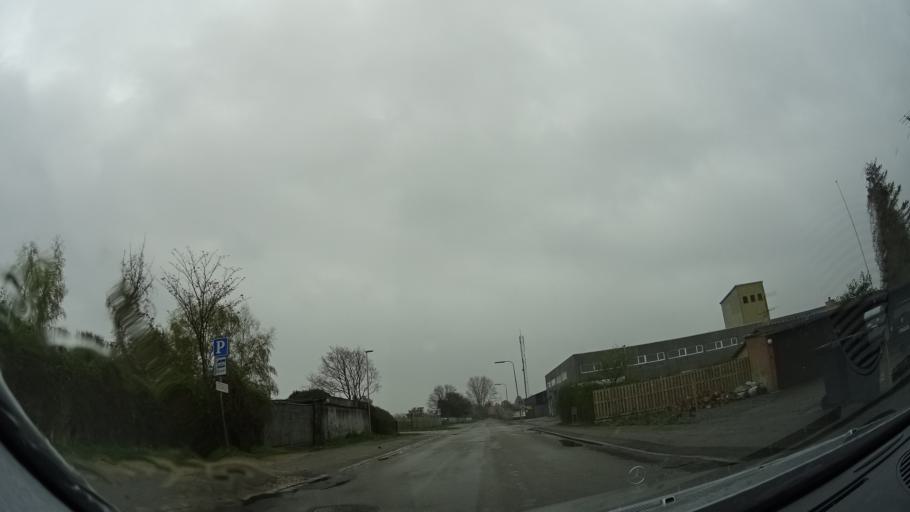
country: DK
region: Zealand
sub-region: Holbaek Kommune
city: Holbaek
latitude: 55.7192
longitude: 11.7241
